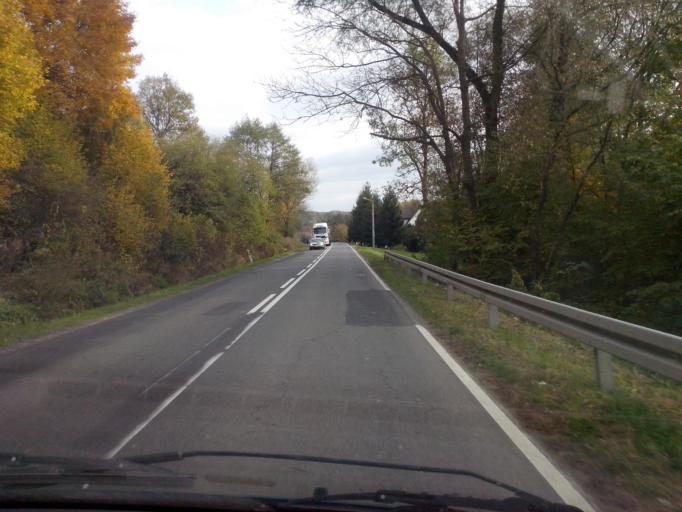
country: PL
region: Subcarpathian Voivodeship
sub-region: Powiat strzyzowski
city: Wisniowa
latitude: 49.9017
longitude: 21.6336
